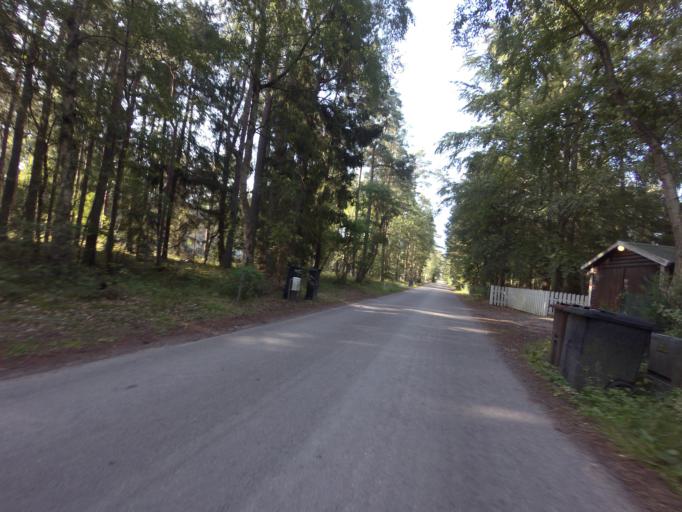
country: SE
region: Skane
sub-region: Landskrona
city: Asmundtorp
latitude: 55.8394
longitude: 12.9321
